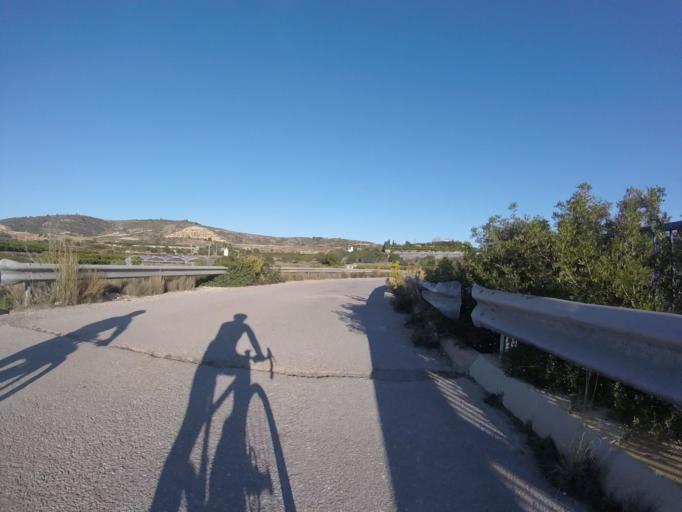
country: ES
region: Valencia
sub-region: Provincia de Castello
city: Torreblanca
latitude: 40.2265
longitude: 0.1981
